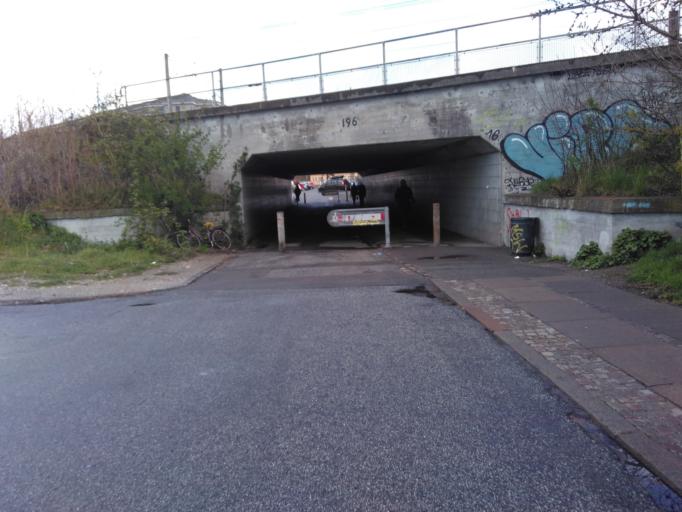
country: DK
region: Capital Region
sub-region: Frederiksberg Kommune
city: Frederiksberg
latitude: 55.6511
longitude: 12.5207
